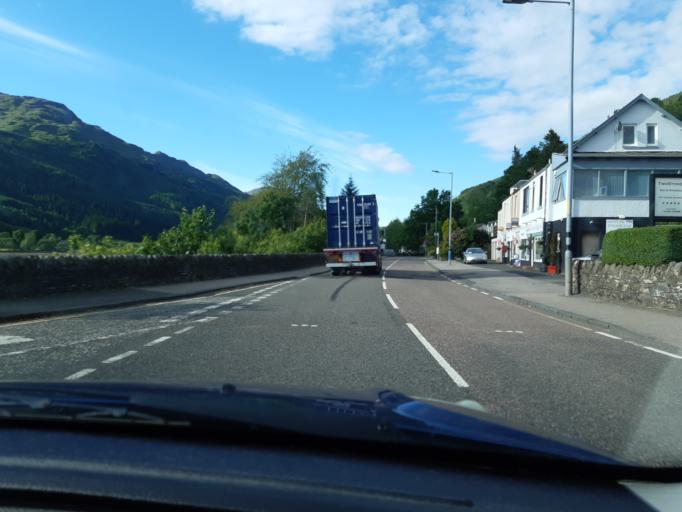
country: GB
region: Scotland
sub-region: Argyll and Bute
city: Garelochhead
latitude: 56.2010
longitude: -4.7454
